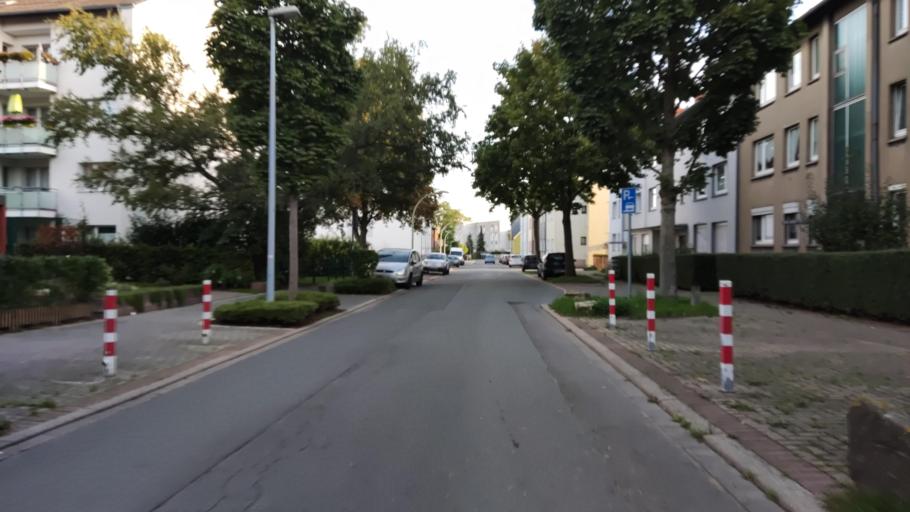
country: DE
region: North Rhine-Westphalia
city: Castrop-Rauxel
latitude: 51.5478
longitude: 7.2850
